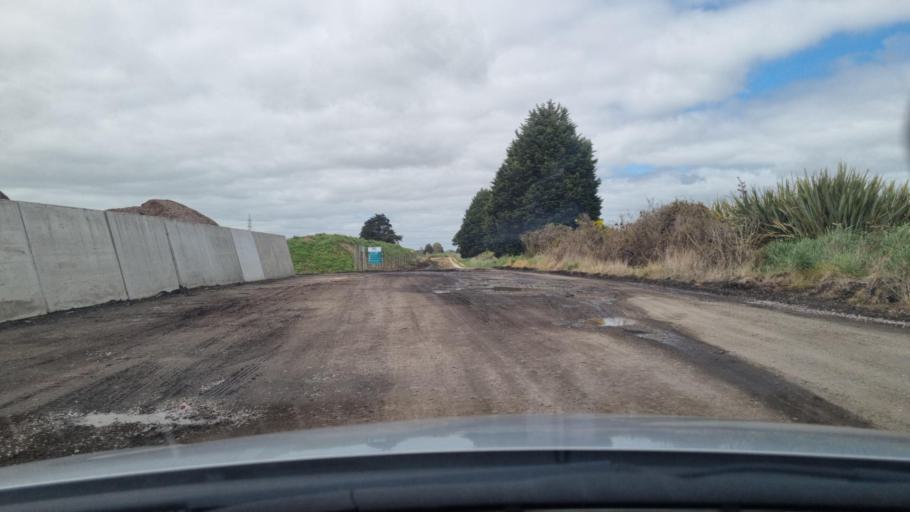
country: NZ
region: Southland
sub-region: Invercargill City
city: Invercargill
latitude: -46.3922
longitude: 168.4560
